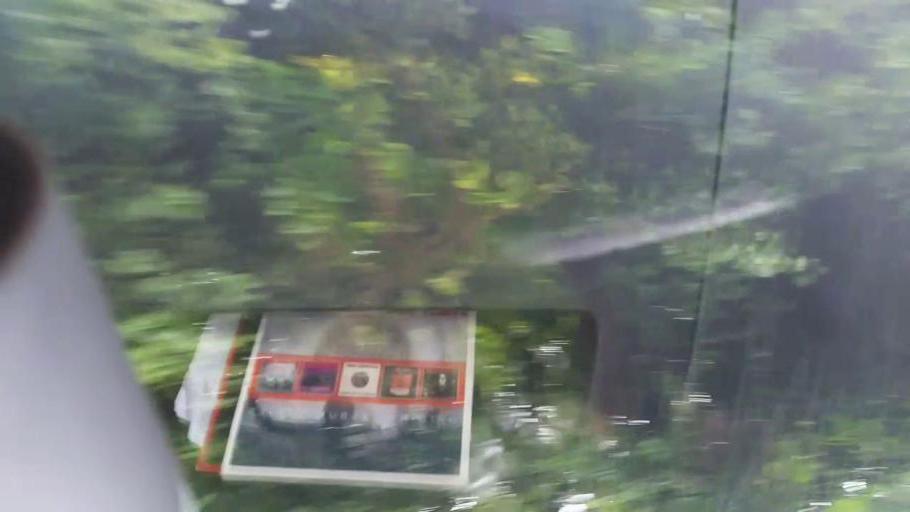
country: NZ
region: Auckland
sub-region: Auckland
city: Waitakere
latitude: -36.9164
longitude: 174.5665
